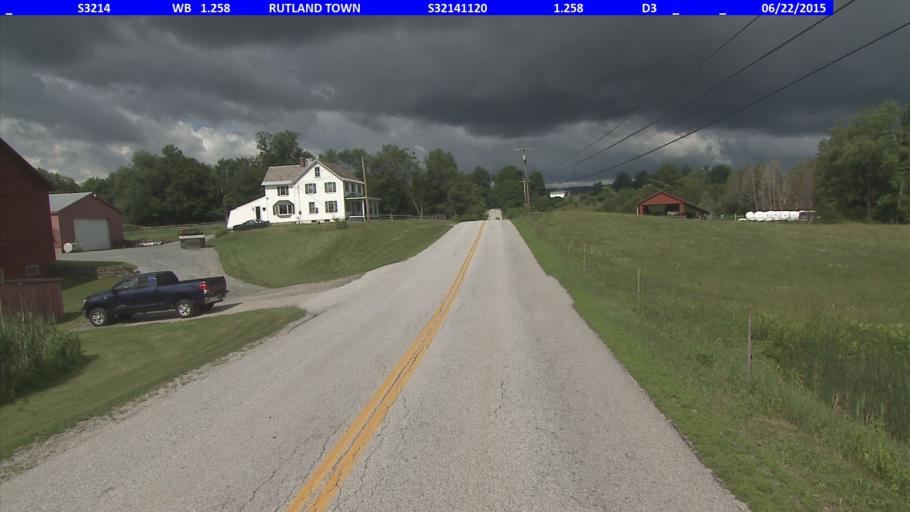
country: US
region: Vermont
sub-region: Rutland County
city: Rutland
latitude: 43.6401
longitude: -72.9536
